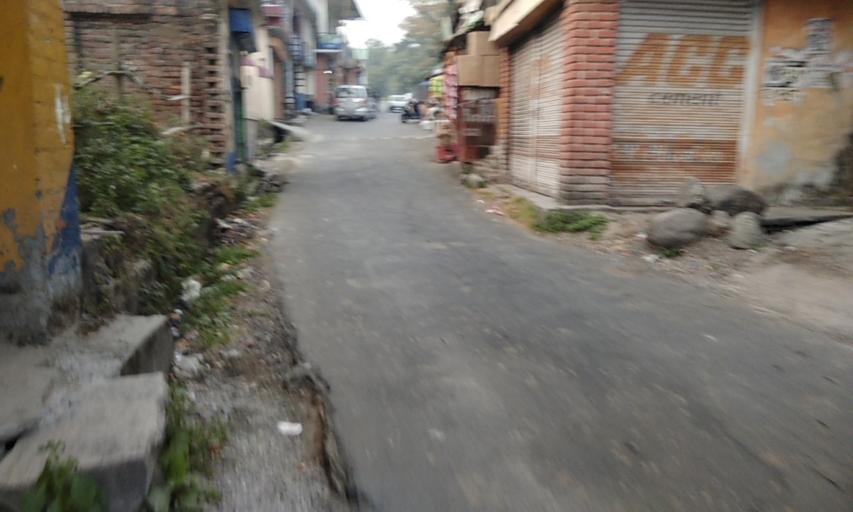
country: IN
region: Himachal Pradesh
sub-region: Kangra
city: Palampur
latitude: 32.1194
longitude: 76.5334
